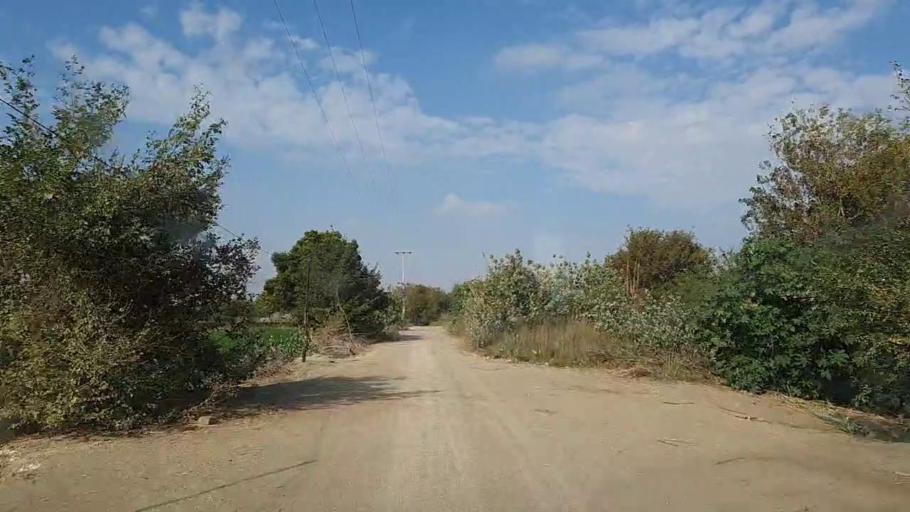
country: PK
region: Sindh
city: Sanghar
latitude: 26.2772
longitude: 69.0092
